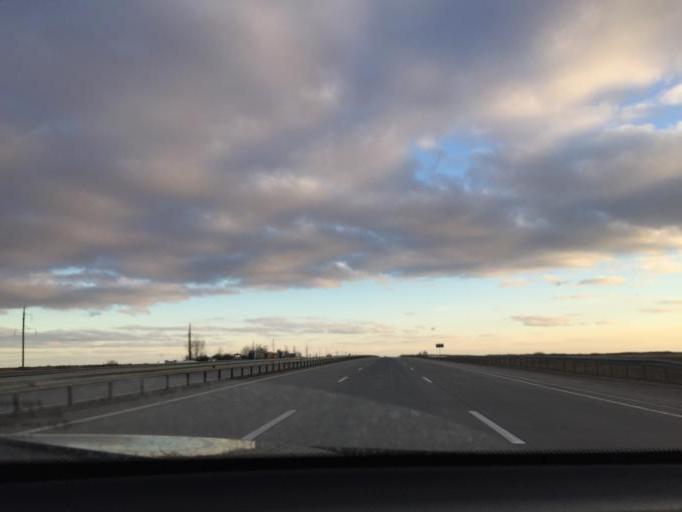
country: KZ
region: Astana Qalasy
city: Astana
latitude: 51.3548
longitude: 71.3350
